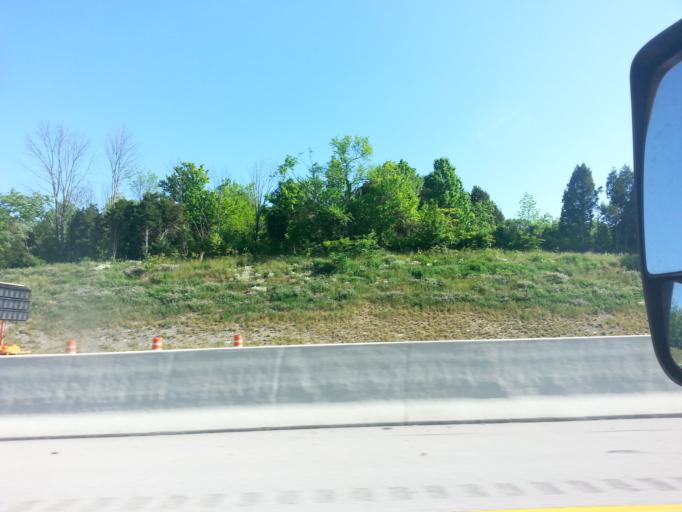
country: US
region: Kentucky
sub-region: Jefferson County
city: Middletown
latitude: 38.2215
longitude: -85.4679
